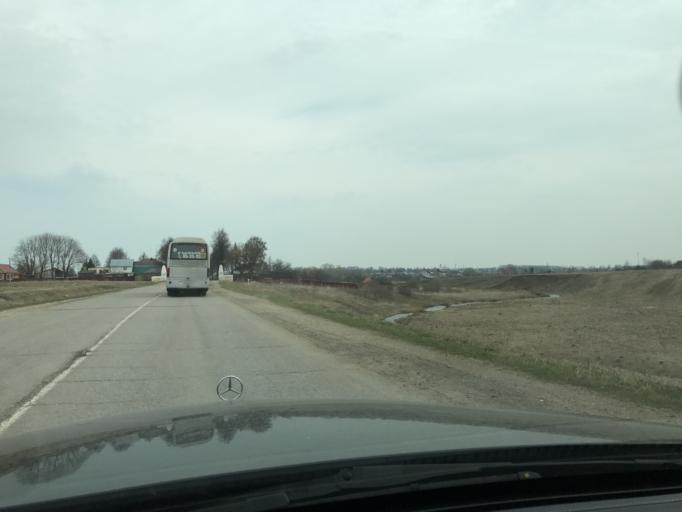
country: RU
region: Vladimir
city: Suzdal'
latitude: 56.4049
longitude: 40.4453
